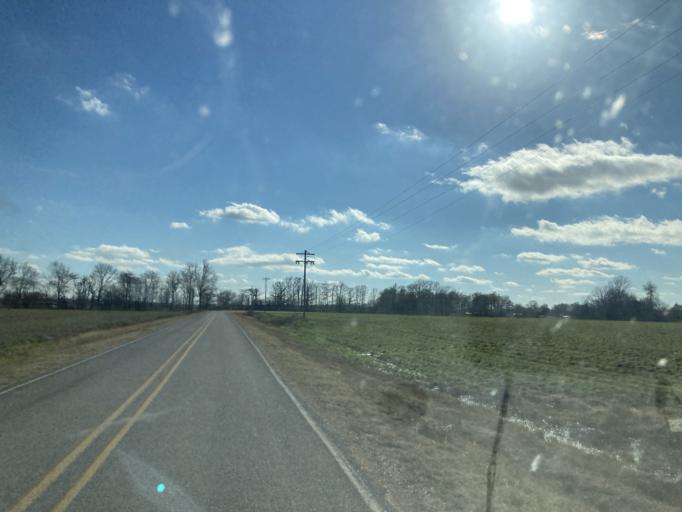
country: US
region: Mississippi
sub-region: Yazoo County
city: Yazoo City
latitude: 32.9615
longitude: -90.4943
